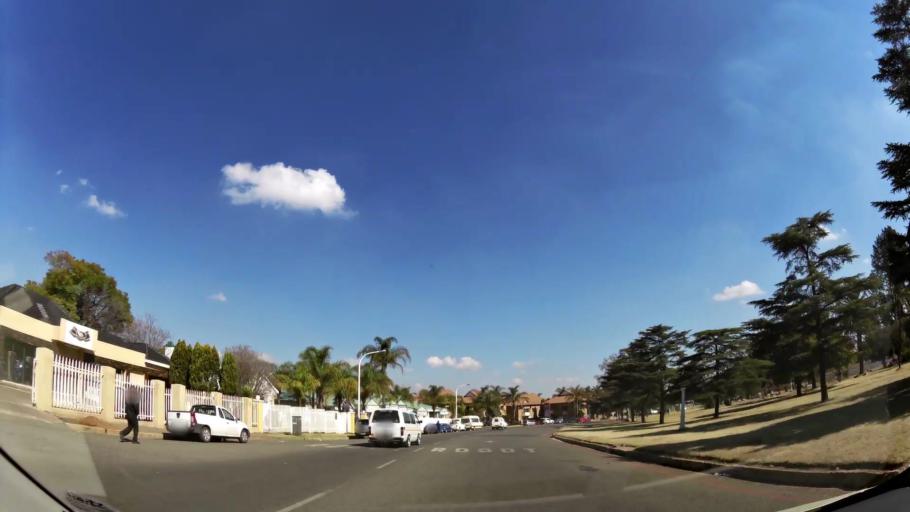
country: ZA
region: Mpumalanga
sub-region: Nkangala District Municipality
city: Witbank
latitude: -25.8760
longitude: 29.2191
